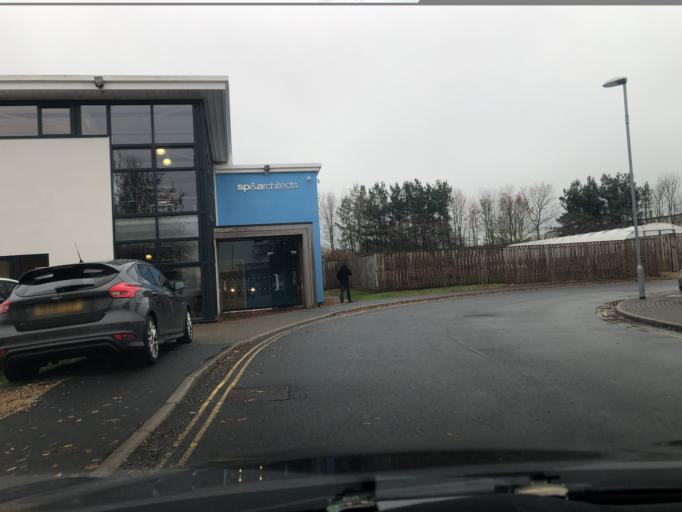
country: GB
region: England
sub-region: North Yorkshire
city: Stokesley
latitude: 54.4609
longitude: -1.1767
